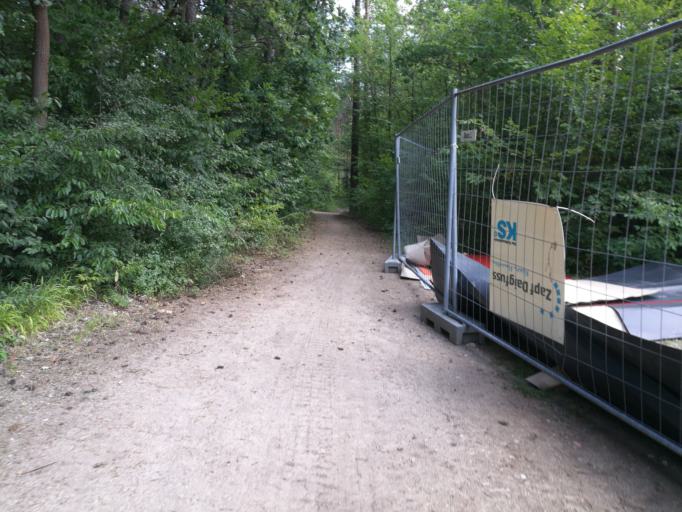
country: DE
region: Bavaria
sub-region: Regierungsbezirk Mittelfranken
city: Heroldsberg
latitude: 49.4847
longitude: 11.1338
